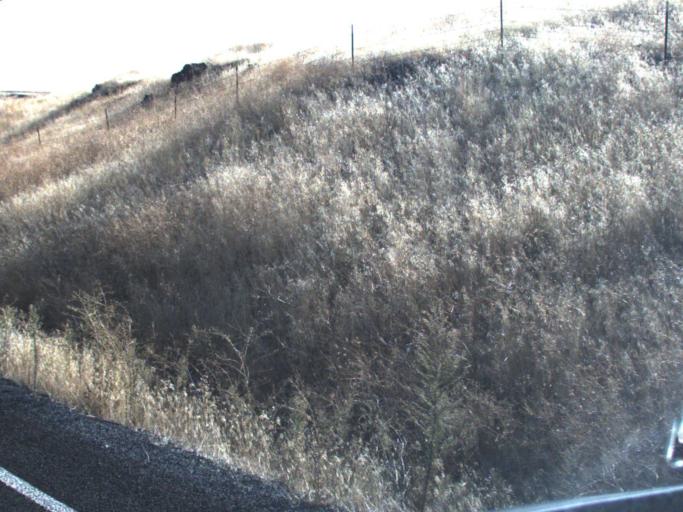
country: US
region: Washington
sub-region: Franklin County
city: Connell
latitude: 46.6359
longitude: -118.6271
